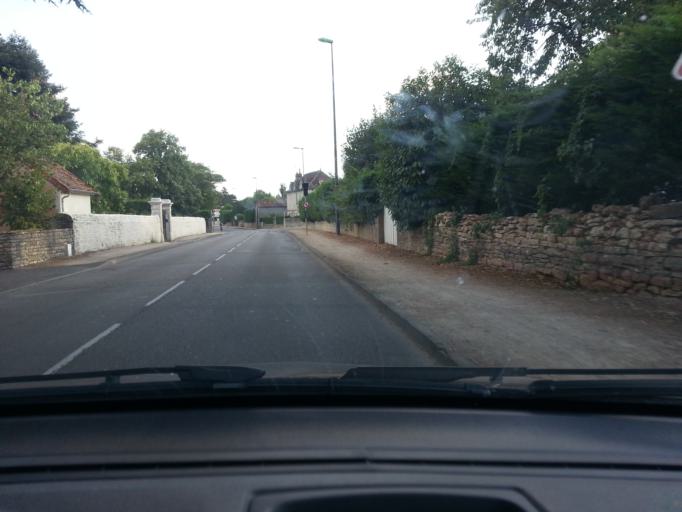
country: FR
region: Bourgogne
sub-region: Departement de Saone-et-Loire
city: Givry
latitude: 46.7786
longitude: 4.7400
